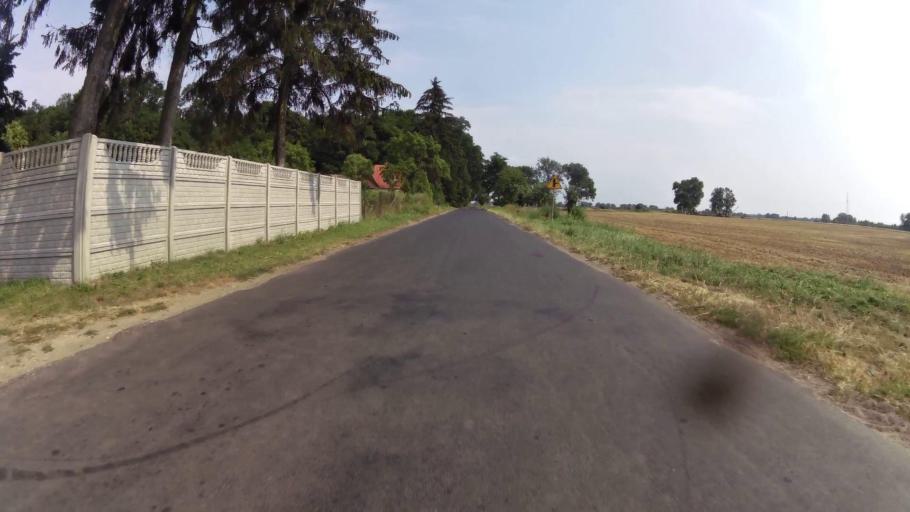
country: PL
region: West Pomeranian Voivodeship
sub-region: Powiat pyrzycki
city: Lipiany
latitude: 52.9700
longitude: 14.9877
